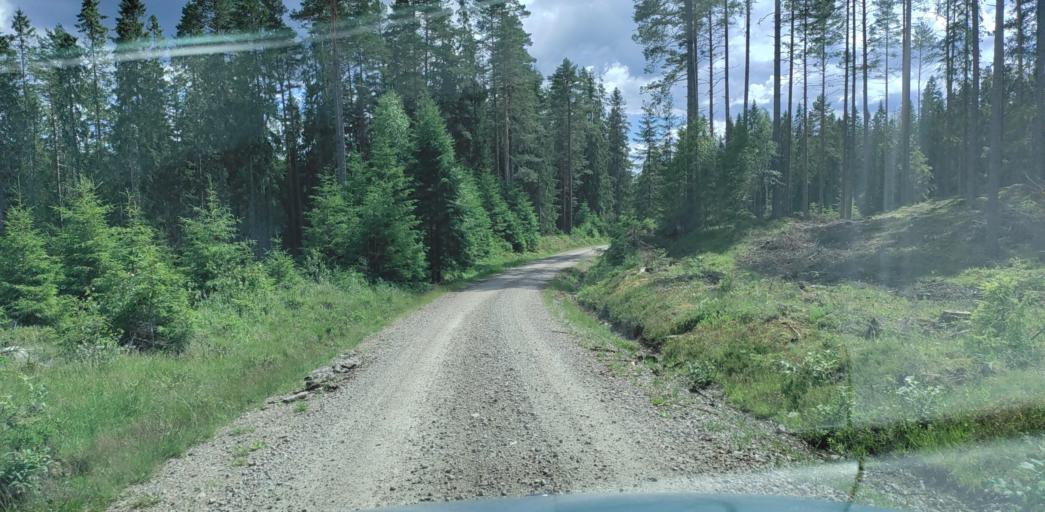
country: SE
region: Vaermland
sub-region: Hagfors Kommun
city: Ekshaerad
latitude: 60.0434
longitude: 13.3118
